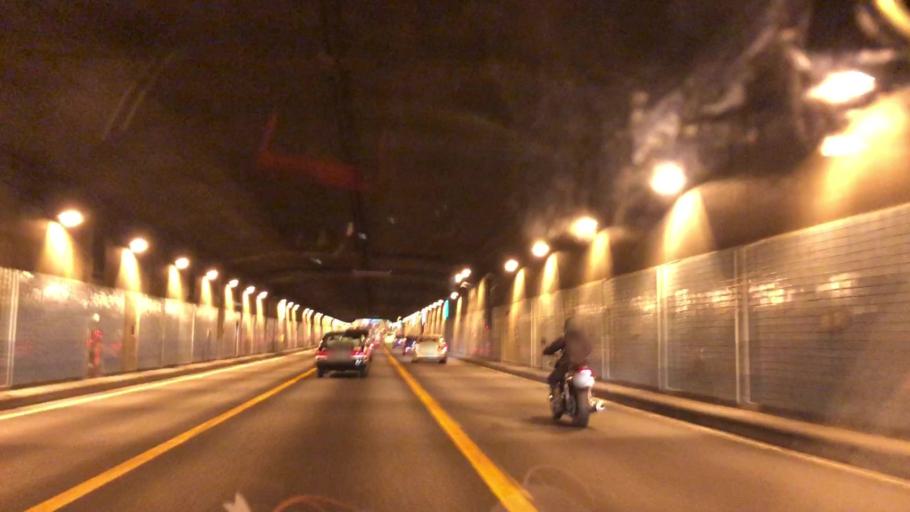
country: JP
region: Tokyo
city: Tokyo
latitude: 35.6173
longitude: 139.7629
